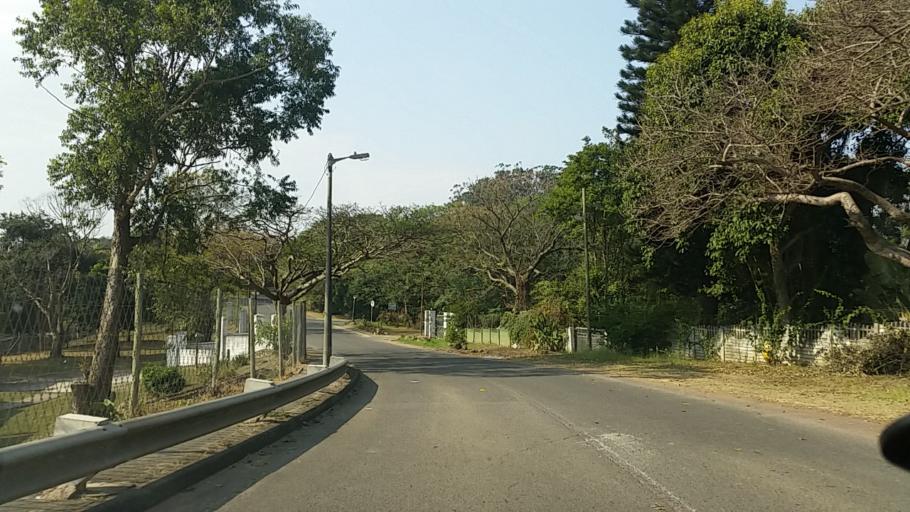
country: ZA
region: KwaZulu-Natal
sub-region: eThekwini Metropolitan Municipality
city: Berea
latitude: -29.8451
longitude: 30.9416
